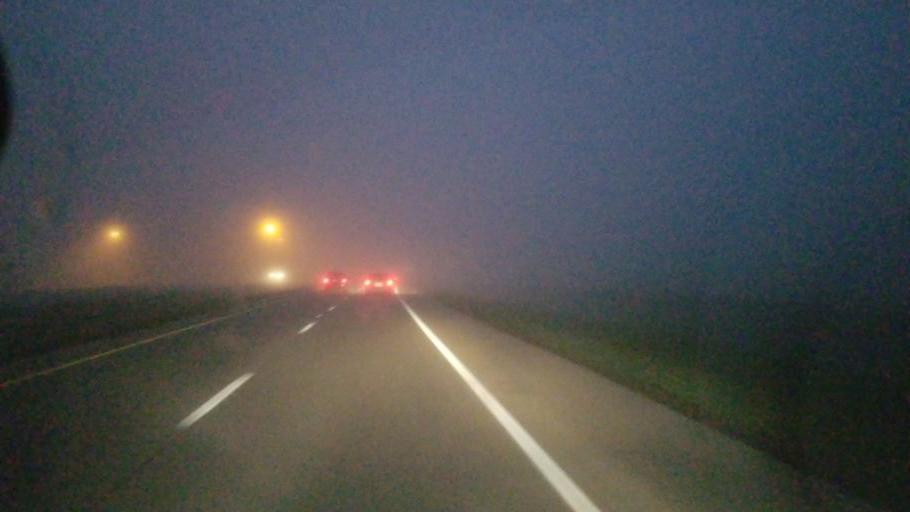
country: US
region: Ohio
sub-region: Ross County
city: Chillicothe
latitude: 39.2902
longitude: -82.9460
